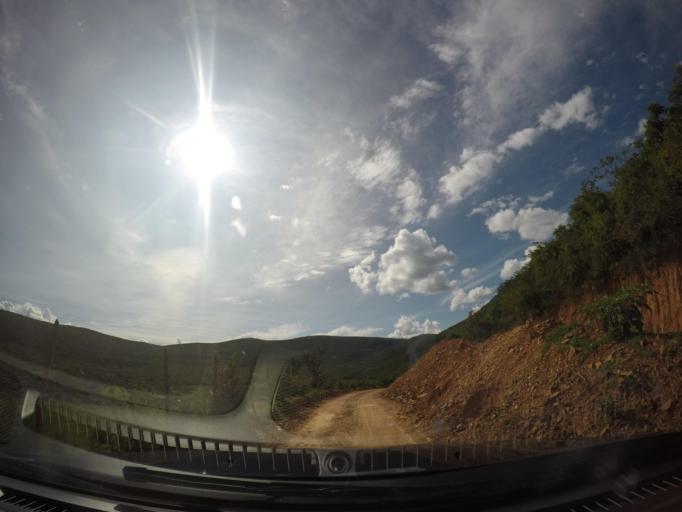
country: BR
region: Bahia
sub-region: Barra Da Estiva
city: Barra da Estiva
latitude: -13.1964
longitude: -41.5906
